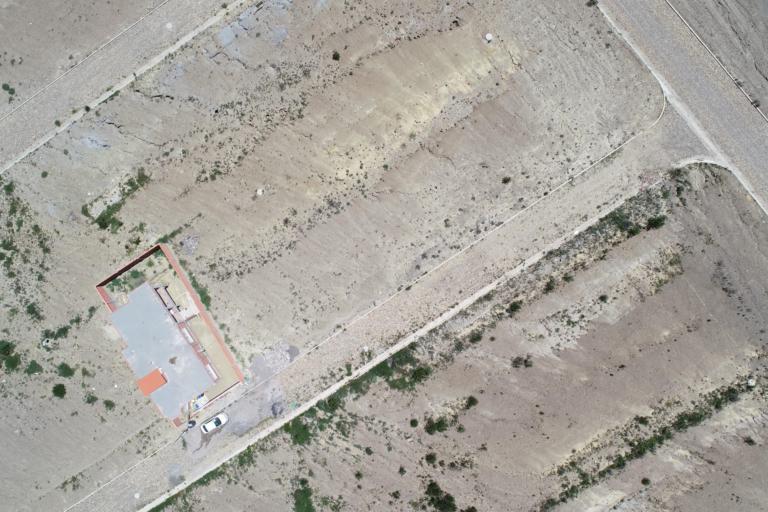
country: BO
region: La Paz
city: La Paz
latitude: -16.5221
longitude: -68.0480
